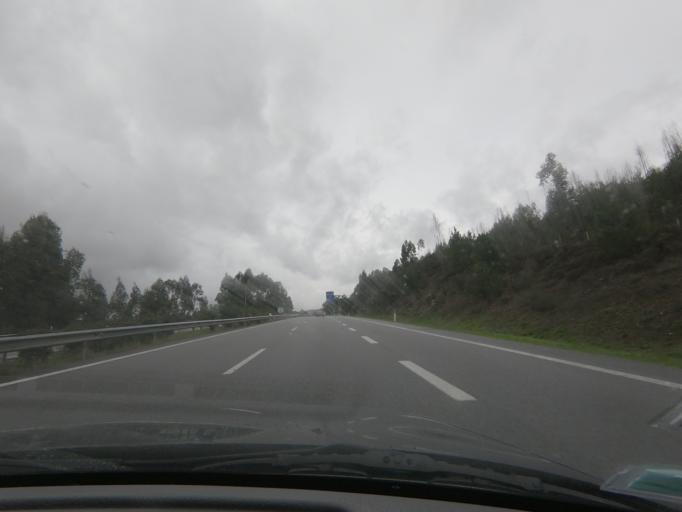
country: PT
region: Porto
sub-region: Valongo
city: Campo
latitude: 41.1917
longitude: -8.4818
